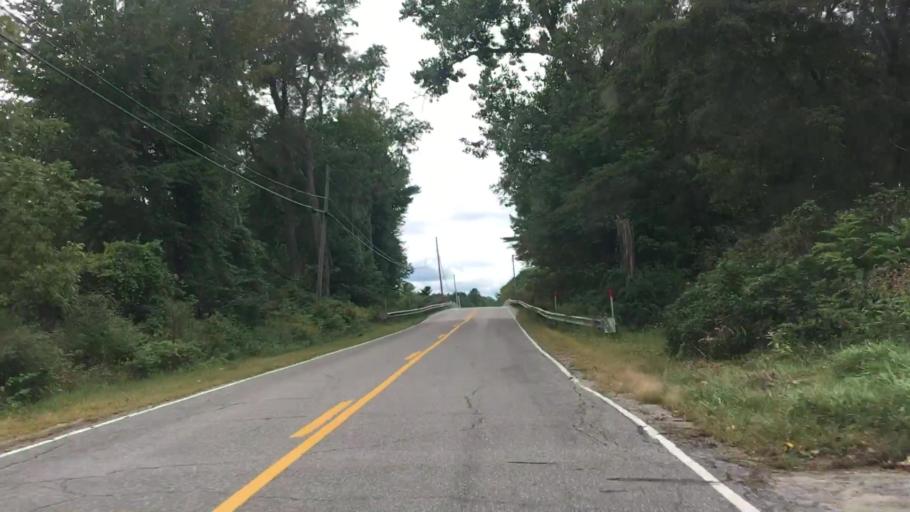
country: US
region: Maine
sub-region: Kennebec County
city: Hallowell
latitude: 44.2772
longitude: -69.8044
